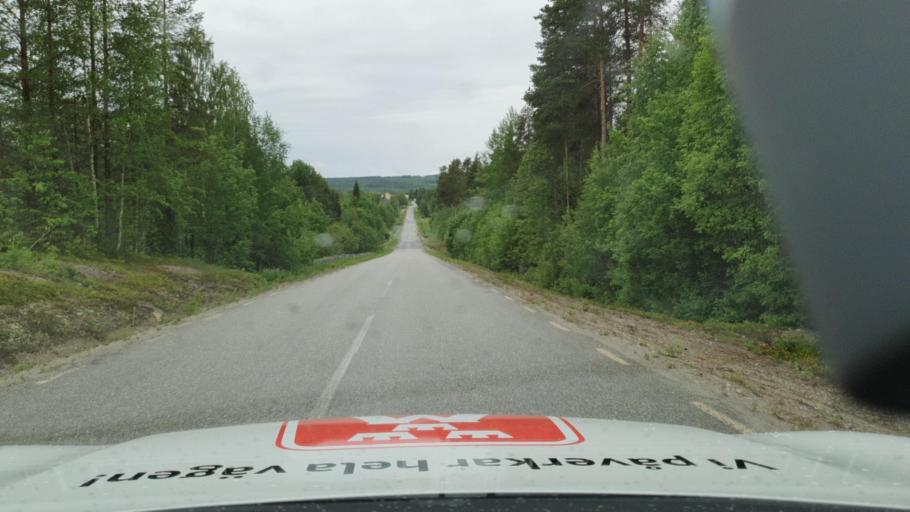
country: SE
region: Vaesterbotten
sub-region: Asele Kommun
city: Asele
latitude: 63.9683
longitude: 17.1176
